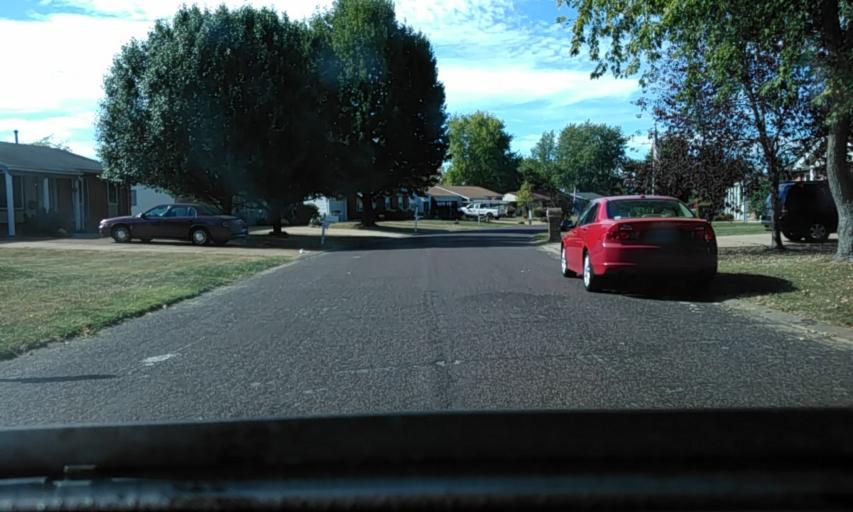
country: US
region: Missouri
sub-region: Saint Louis County
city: Concord
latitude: 38.4814
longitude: -90.3606
